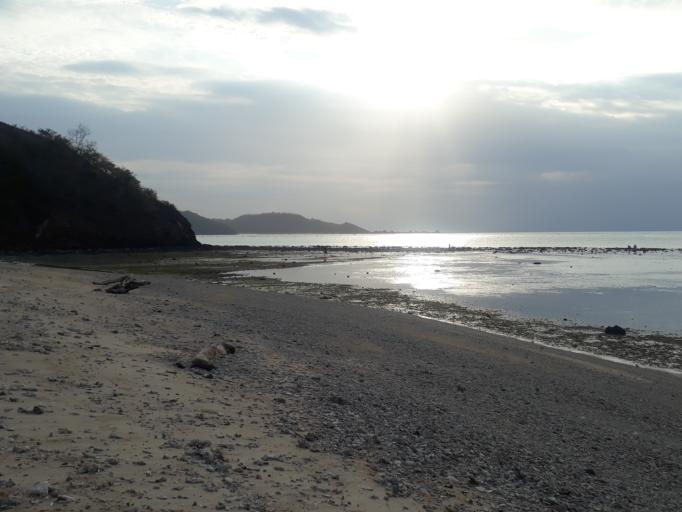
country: ID
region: West Nusa Tenggara
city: Tawun
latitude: -8.7317
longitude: 115.8862
